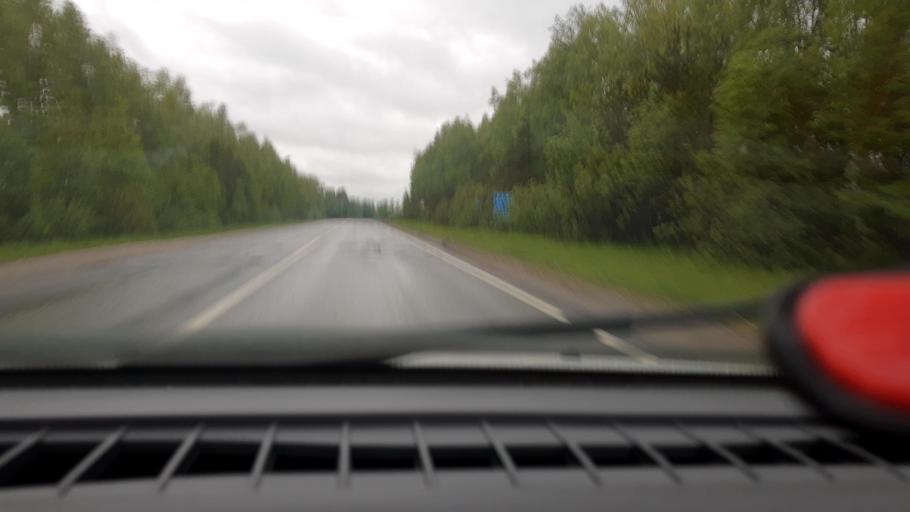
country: RU
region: Nizjnij Novgorod
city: Krasnyye Baki
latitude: 57.0079
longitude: 45.1120
